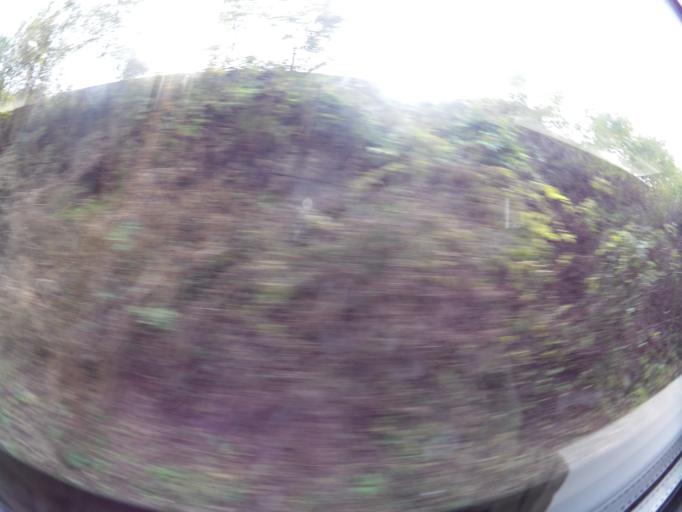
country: KR
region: Chungcheongbuk-do
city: Yong-dong
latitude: 36.1929
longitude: 127.8586
